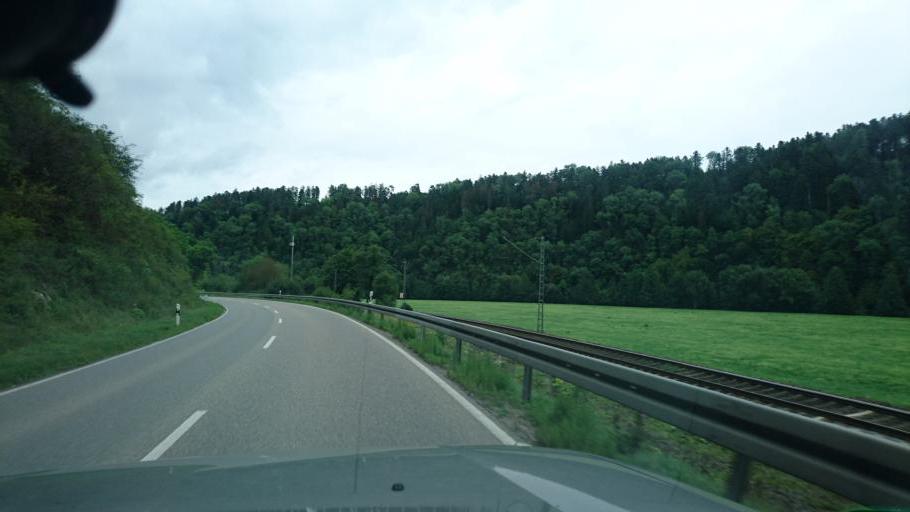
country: DE
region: Baden-Wuerttemberg
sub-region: Freiburg Region
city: Muhlheim am Bach
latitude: 48.3744
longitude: 8.6652
